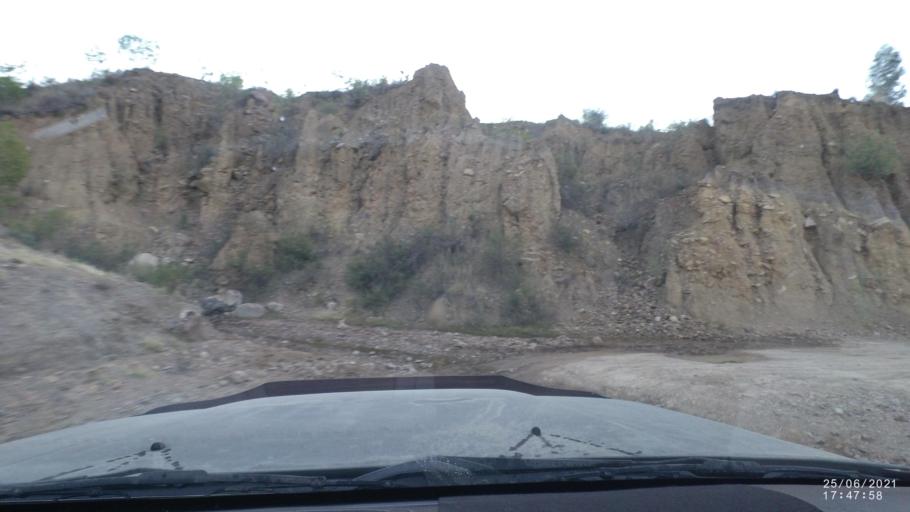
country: BO
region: Cochabamba
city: Mizque
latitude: -17.9596
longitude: -65.6442
